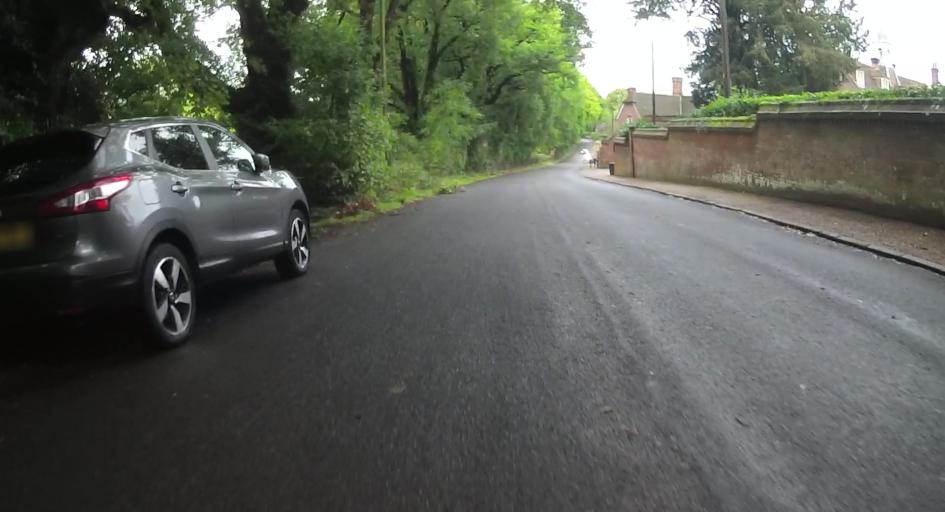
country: GB
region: England
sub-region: Hampshire
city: Tadley
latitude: 51.4034
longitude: -1.1736
